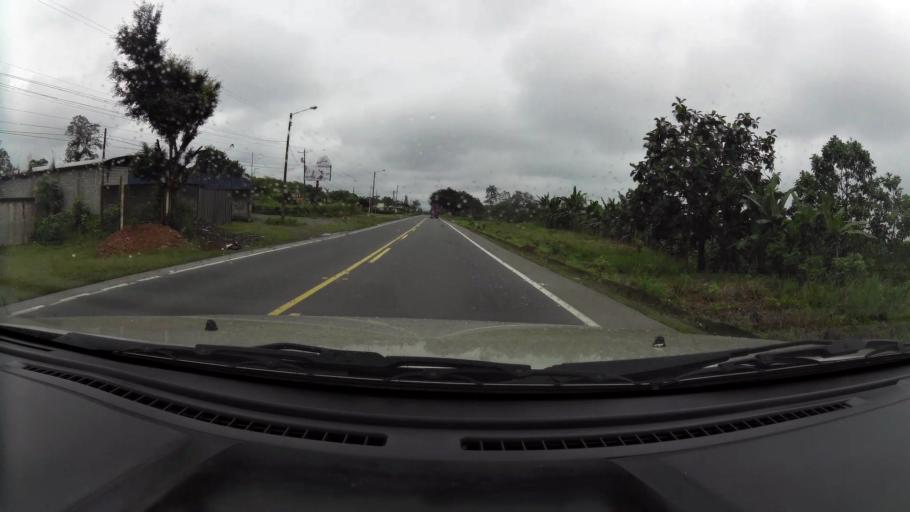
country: EC
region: Santo Domingo de los Tsachilas
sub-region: Canton Santo Domingo de los Colorados
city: Santo Domingo de los Colorados
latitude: -0.2707
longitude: -79.1535
